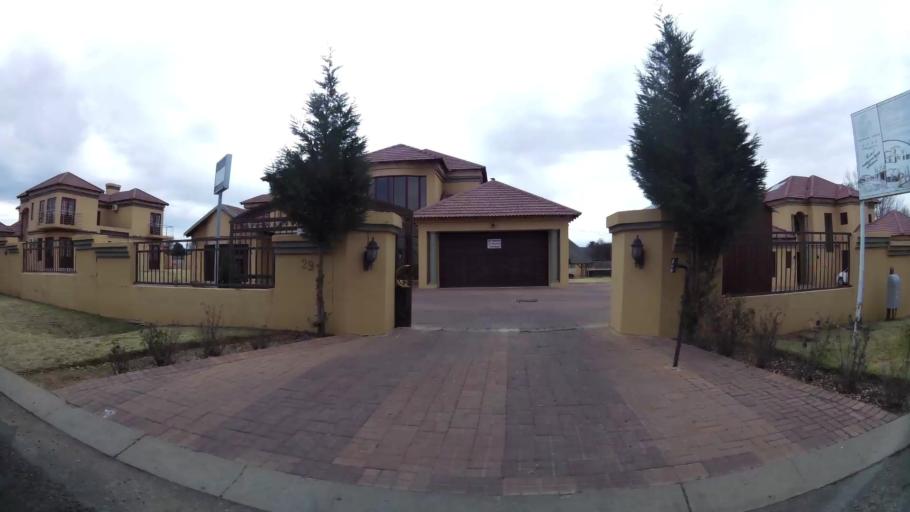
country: ZA
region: Orange Free State
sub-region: Fezile Dabi District Municipality
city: Kroonstad
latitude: -27.6282
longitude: 27.2428
